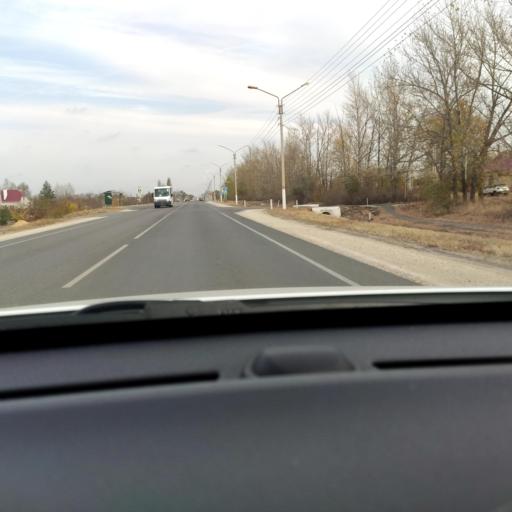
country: RU
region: Voronezj
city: Novaya Usman'
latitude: 51.6552
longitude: 39.4318
